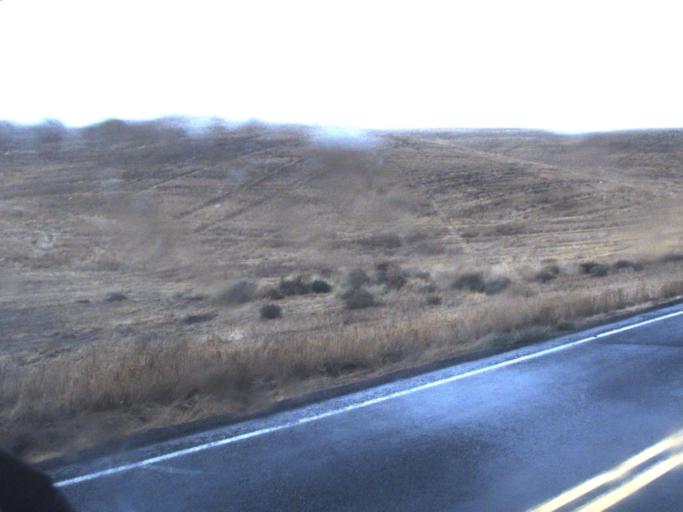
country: US
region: Washington
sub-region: Spokane County
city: Cheney
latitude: 47.1986
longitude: -117.8813
